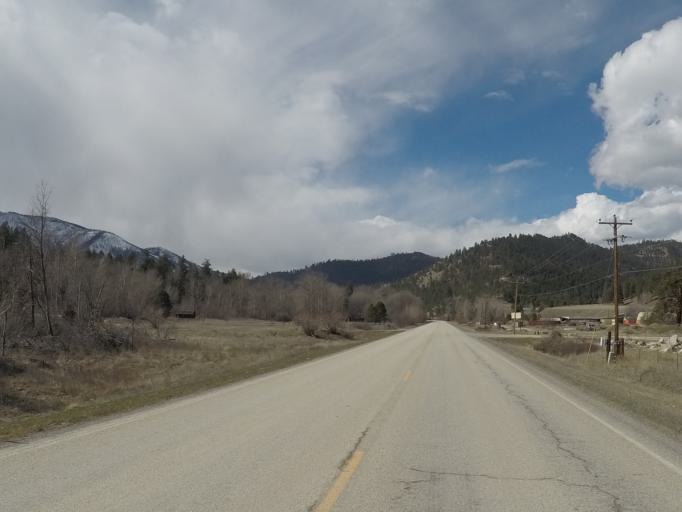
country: US
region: Montana
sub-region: Missoula County
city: Lolo
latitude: 46.7568
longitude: -114.1089
